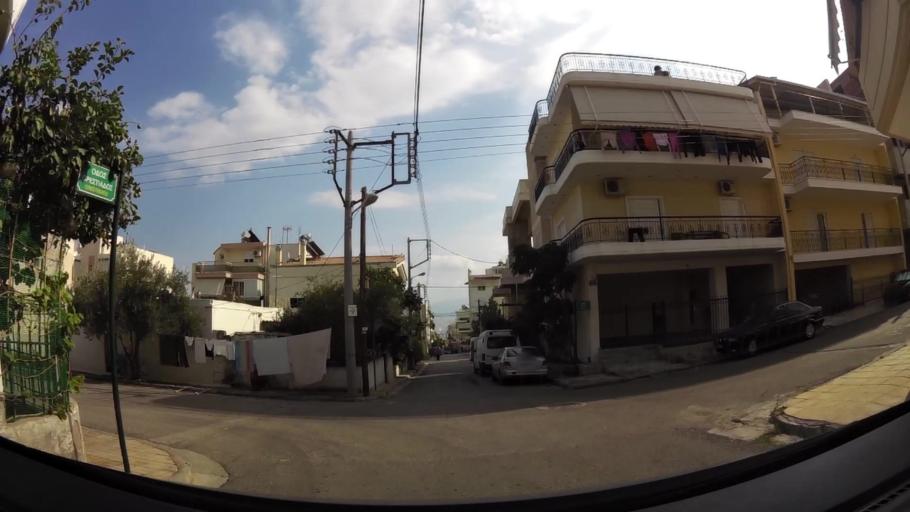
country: GR
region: Attica
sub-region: Nomarchia Athinas
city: Petroupolis
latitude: 38.0488
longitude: 23.6879
